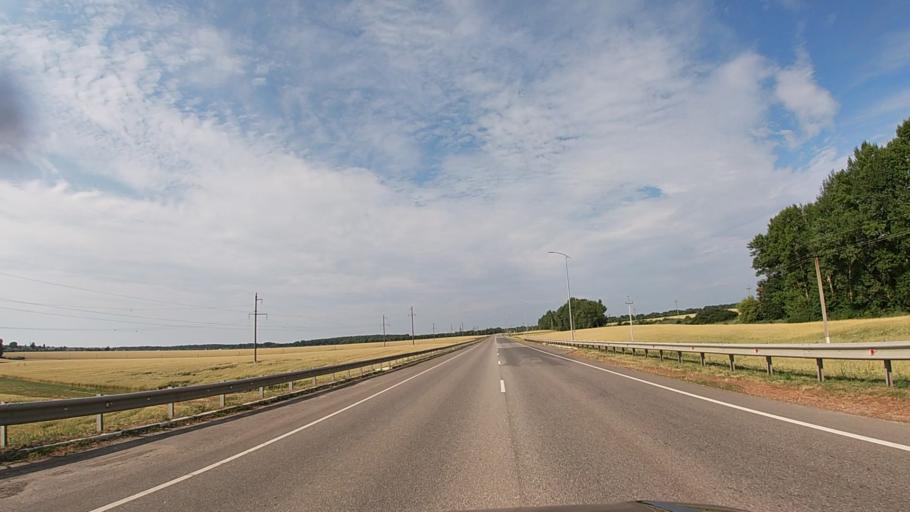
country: RU
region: Belgorod
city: Proletarskiy
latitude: 50.8117
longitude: 35.7481
